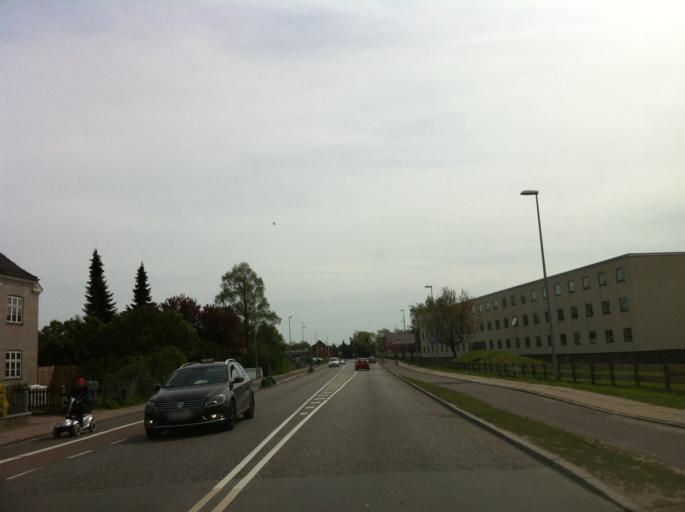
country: DK
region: Zealand
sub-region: Naestved Kommune
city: Naestved
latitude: 55.2517
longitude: 11.7582
